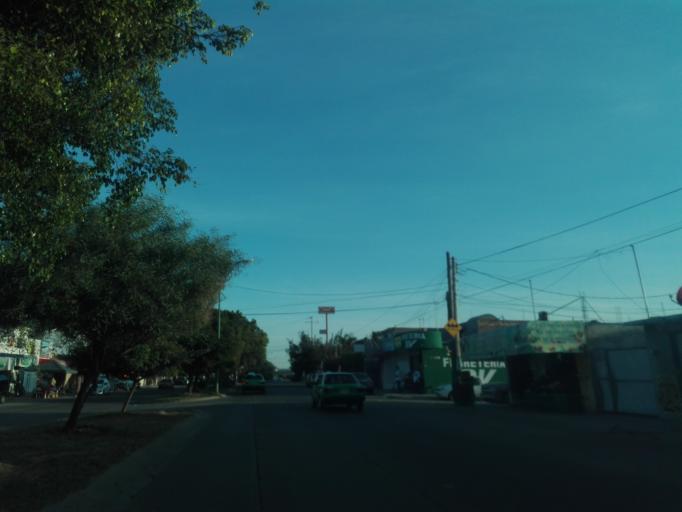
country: MX
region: Guanajuato
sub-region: Leon
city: San Jose de Duran (Los Troncoso)
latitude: 21.0805
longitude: -101.6399
